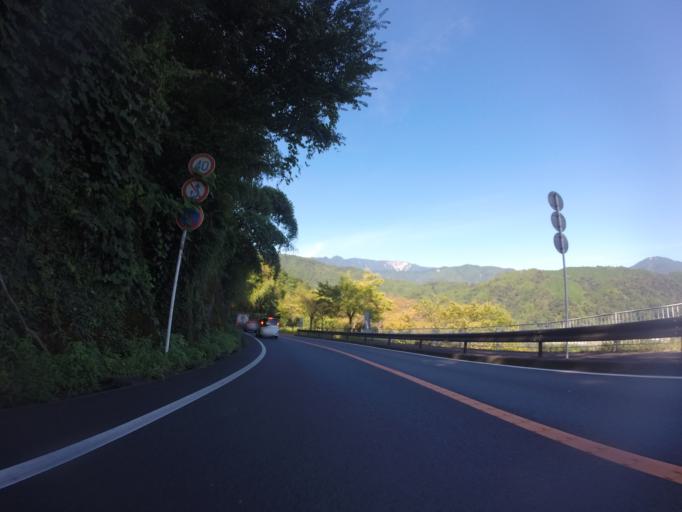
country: JP
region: Shizuoka
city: Fujinomiya
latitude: 35.3534
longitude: 138.4514
